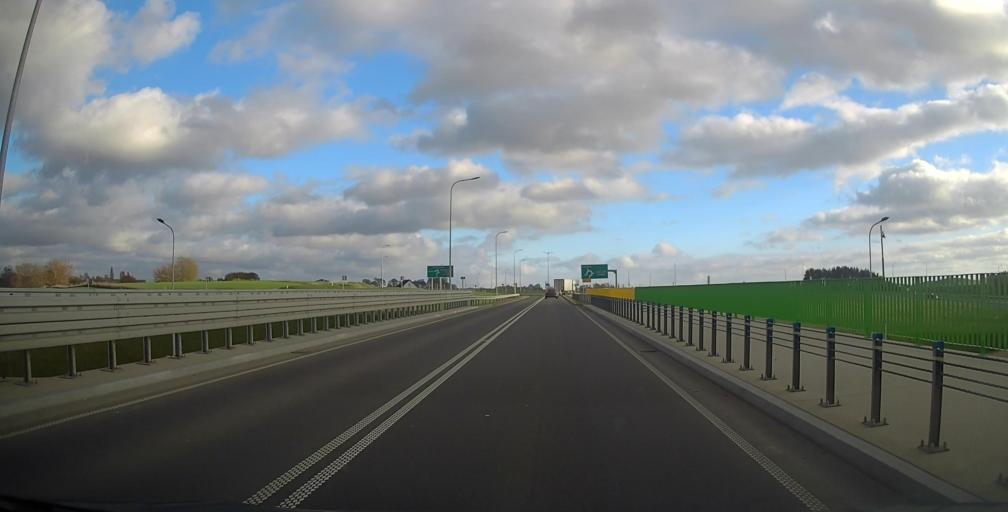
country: PL
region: Podlasie
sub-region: Powiat lomzynski
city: Piatnica
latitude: 53.2500
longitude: 22.1056
